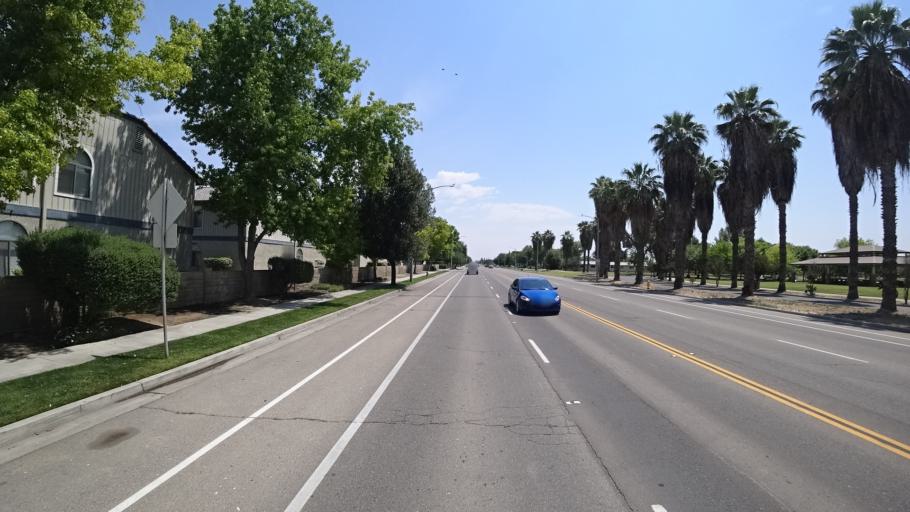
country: US
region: California
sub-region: Kings County
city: Lemoore
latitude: 36.3135
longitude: -119.7733
